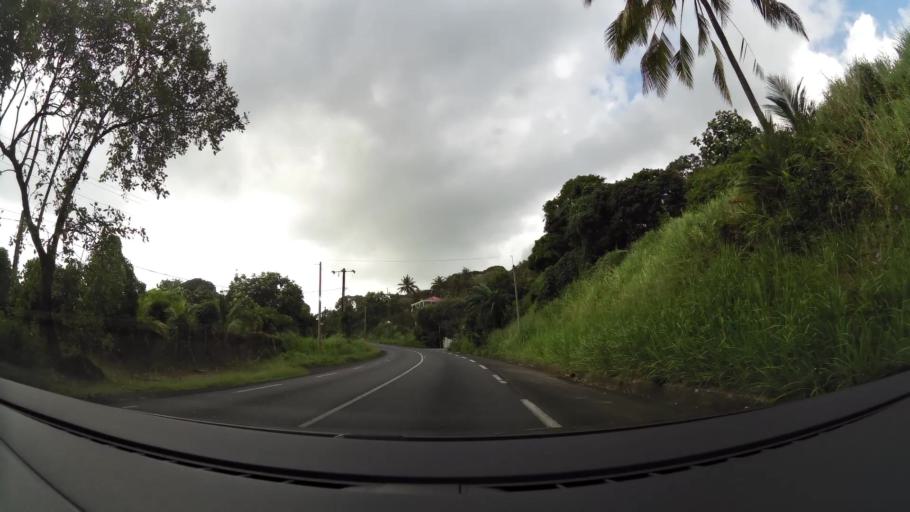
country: GP
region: Guadeloupe
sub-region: Guadeloupe
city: Trois-Rivieres
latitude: 15.9974
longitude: -61.6065
